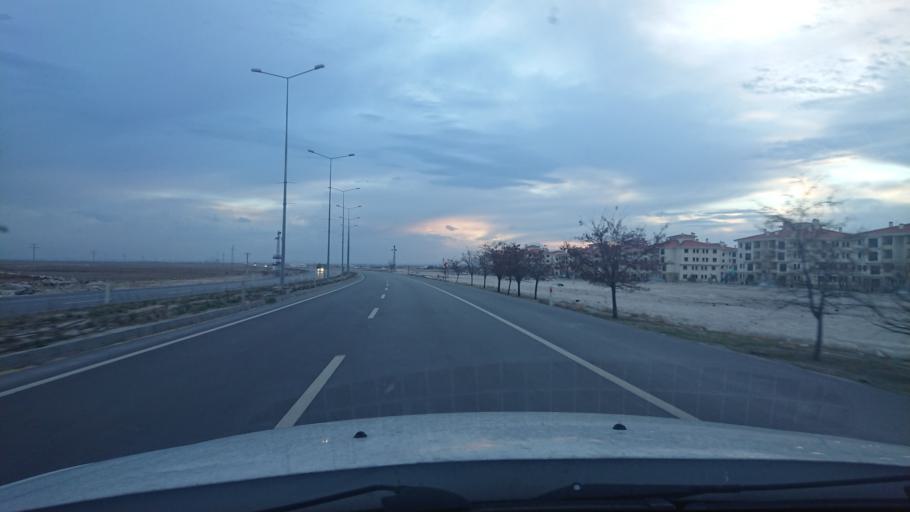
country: TR
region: Aksaray
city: Sultanhani
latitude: 38.2520
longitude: 33.5679
